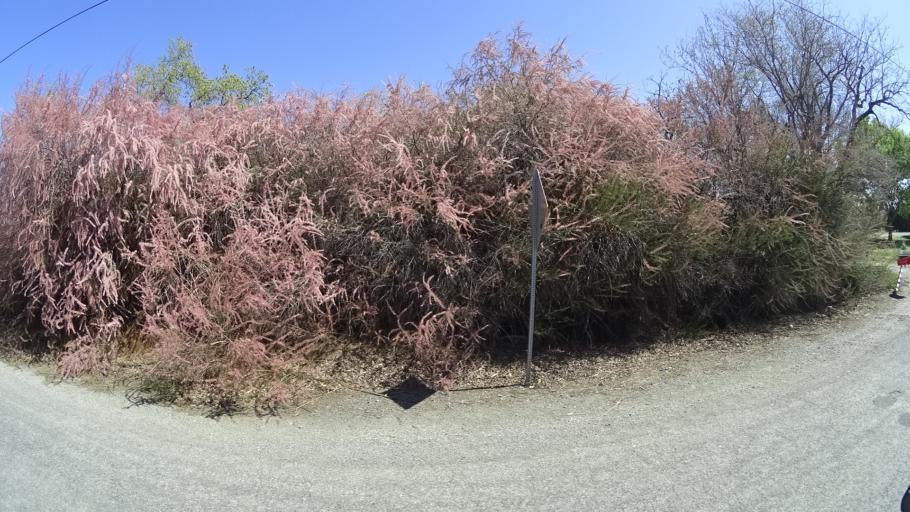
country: US
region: California
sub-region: Glenn County
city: Orland
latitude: 39.7691
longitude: -122.2387
